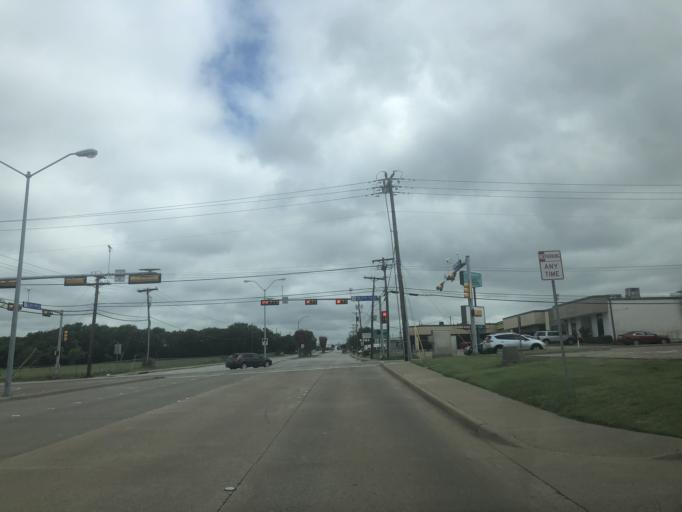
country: US
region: Texas
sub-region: Dallas County
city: Duncanville
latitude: 32.6416
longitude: -96.9252
